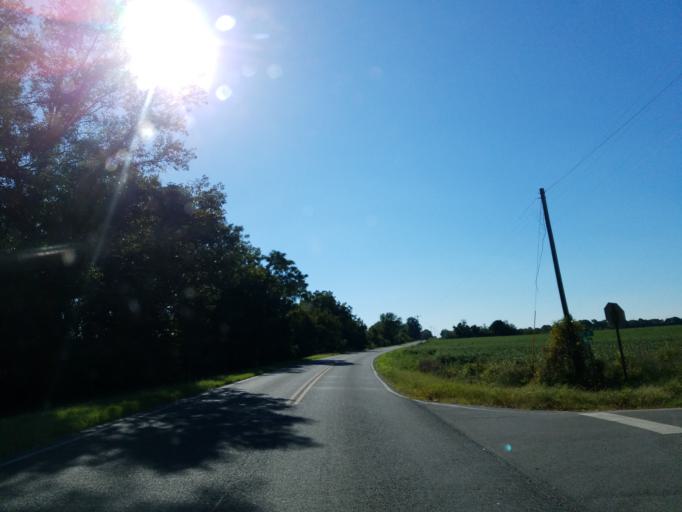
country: US
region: Georgia
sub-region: Dooly County
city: Unadilla
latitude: 32.2583
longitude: -83.7593
